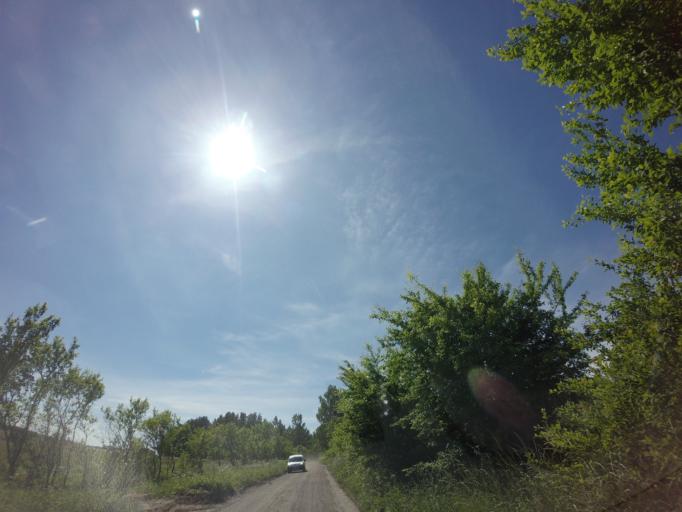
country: PL
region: West Pomeranian Voivodeship
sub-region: Powiat choszczenski
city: Drawno
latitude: 53.2342
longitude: 15.7533
